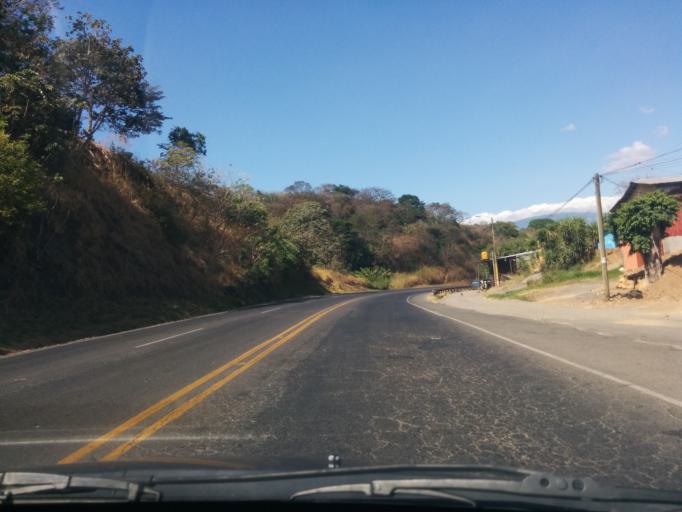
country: CR
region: Alajuela
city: Atenas
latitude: 10.0171
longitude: -84.3397
